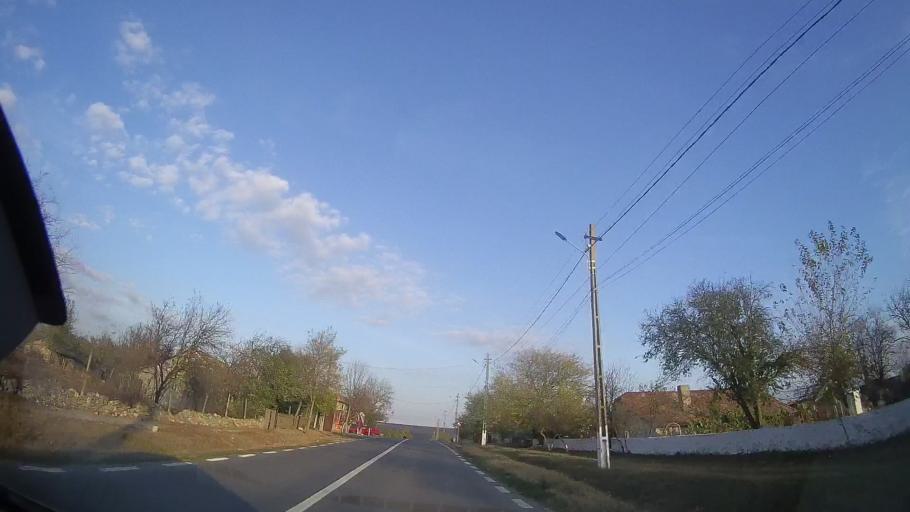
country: RO
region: Constanta
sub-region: Comuna Chirnogeni
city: Plopeni
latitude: 43.9507
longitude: 28.1871
